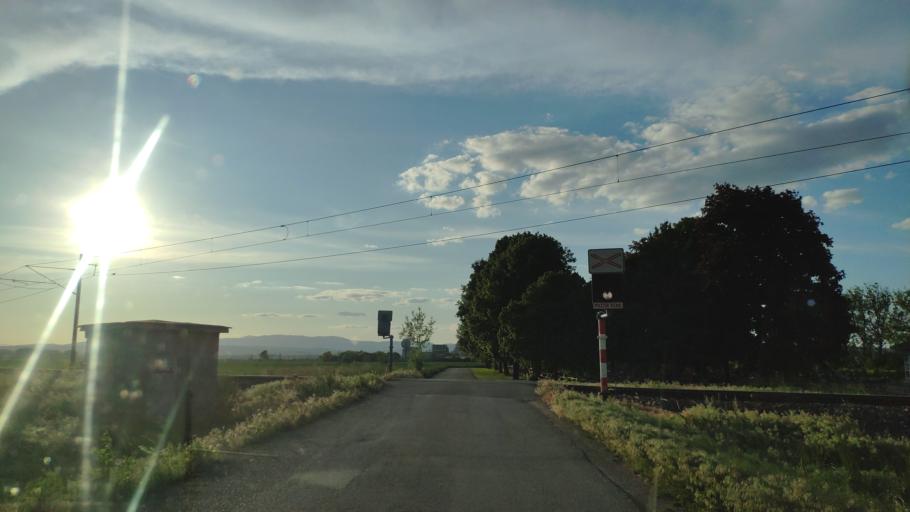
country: SK
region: Kosicky
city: Kosice
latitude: 48.6508
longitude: 21.3191
